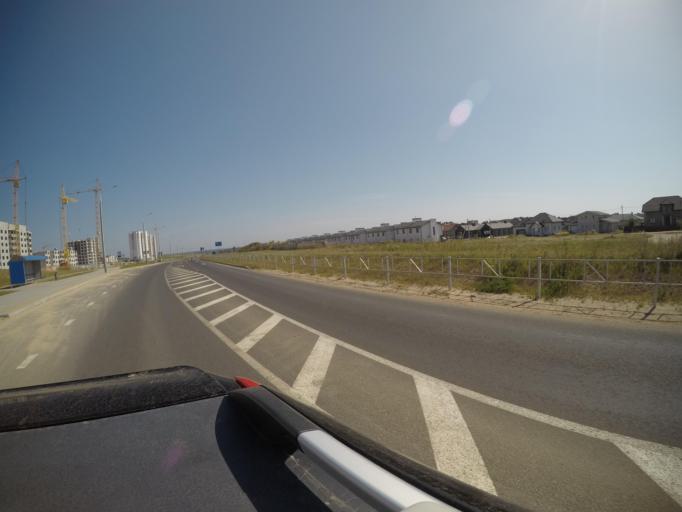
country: BY
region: Grodnenskaya
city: Hrodna
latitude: 53.7158
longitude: 23.8761
